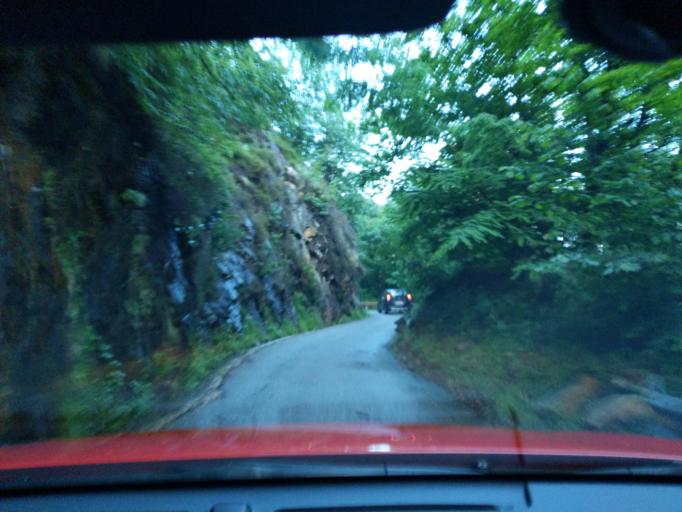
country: IT
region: Piedmont
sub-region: Provincia Verbano-Cusio-Ossola
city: Falmenta
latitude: 46.0916
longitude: 8.5962
